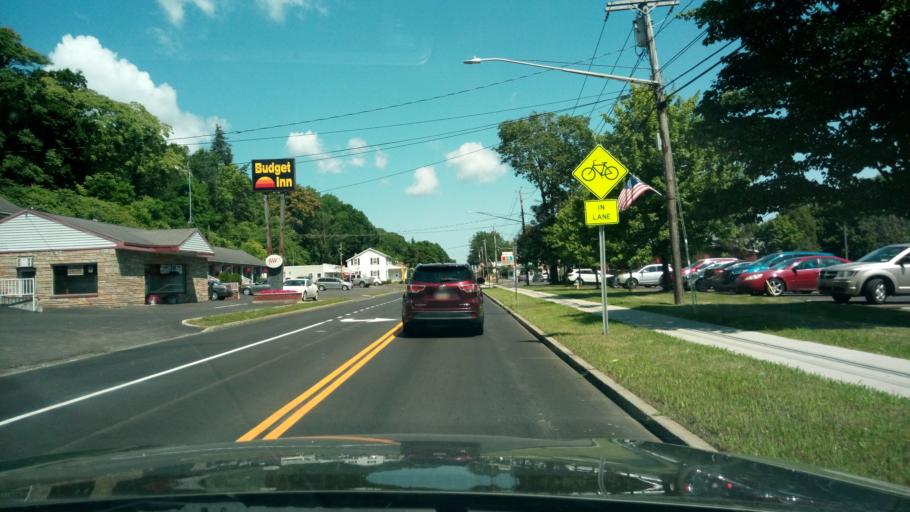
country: US
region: New York
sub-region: Schuyler County
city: Watkins Glen
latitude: 42.3695
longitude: -76.8675
